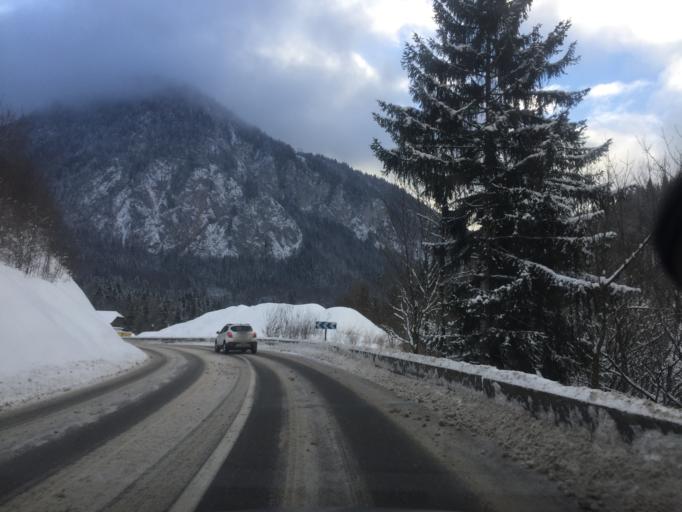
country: FR
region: Rhone-Alpes
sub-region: Departement de la Haute-Savoie
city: Abondance
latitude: 46.3133
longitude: 6.6756
